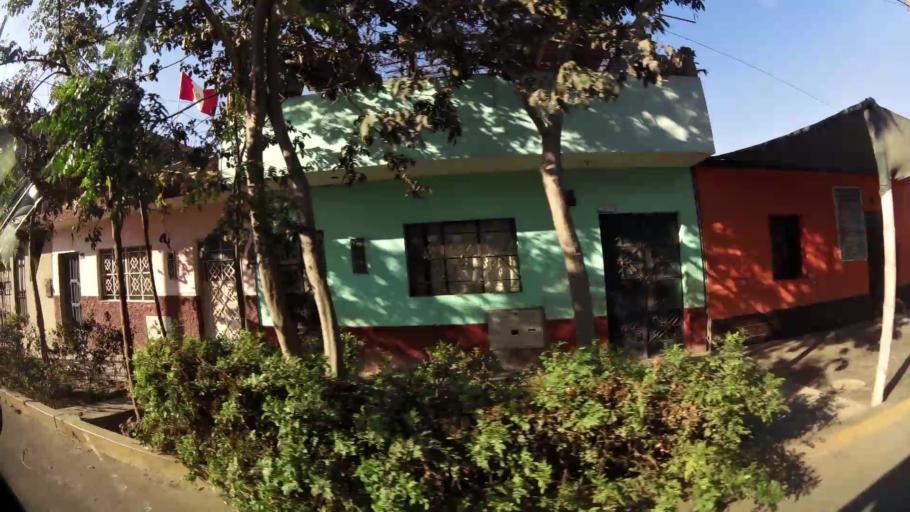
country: PE
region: Ica
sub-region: Provincia de Ica
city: La Tinguina
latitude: -14.0485
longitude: -75.6995
